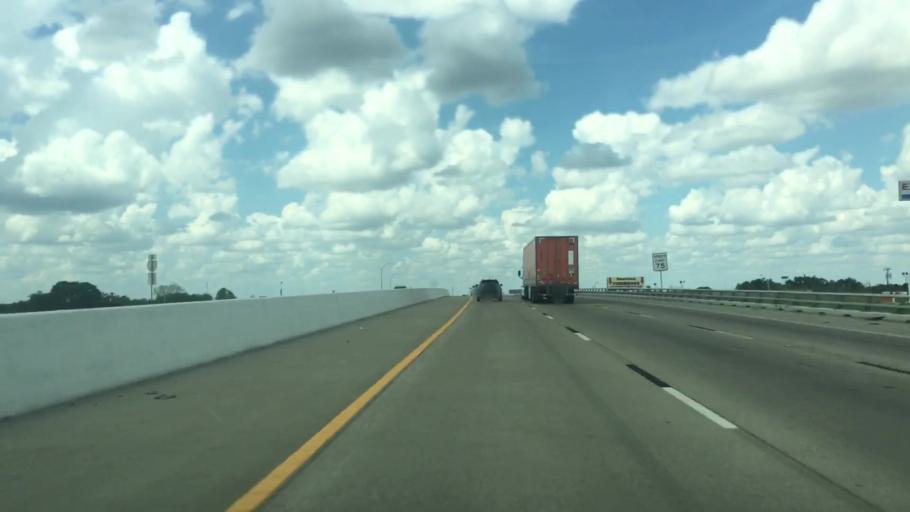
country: US
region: Texas
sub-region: McLennan County
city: Northcrest
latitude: 31.6701
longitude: -97.0991
